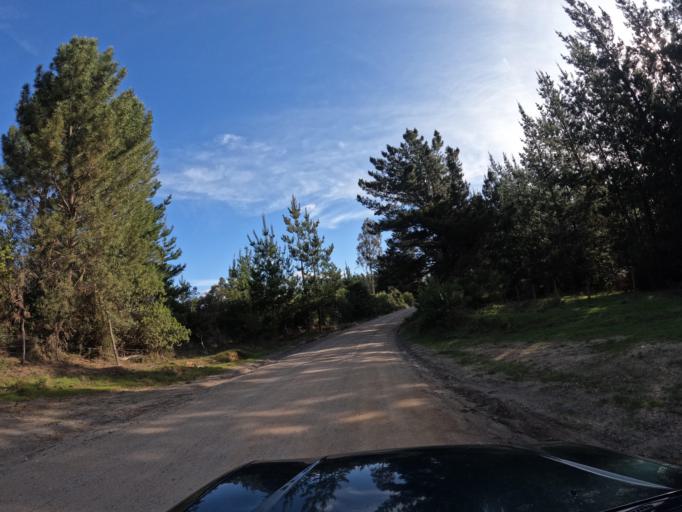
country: CL
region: Biobio
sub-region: Provincia de Biobio
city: La Laja
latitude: -37.1581
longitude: -72.7283
